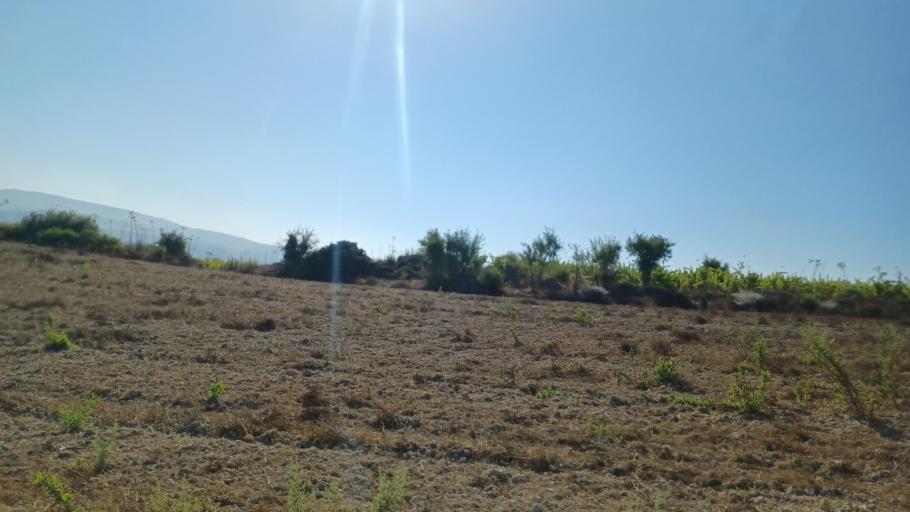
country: CY
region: Pafos
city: Mesogi
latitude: 34.8626
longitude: 32.5162
